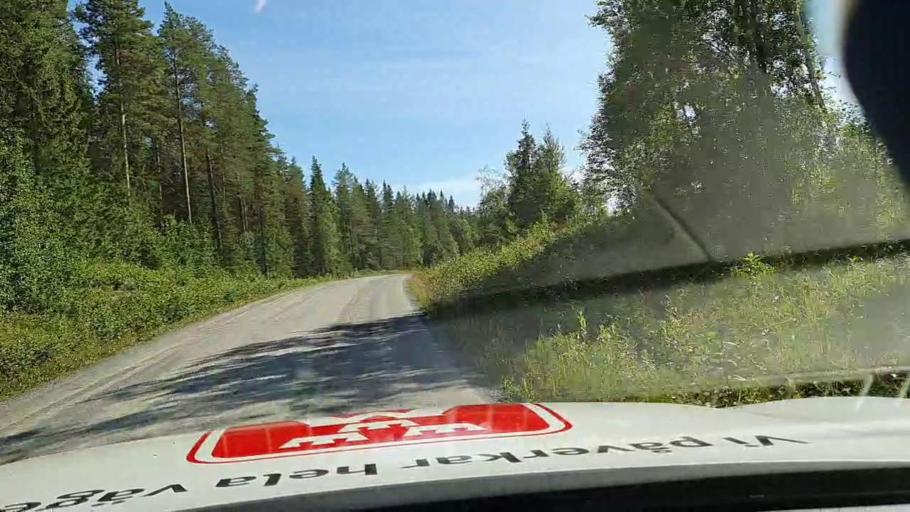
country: SE
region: Jaemtland
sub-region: Krokoms Kommun
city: Krokom
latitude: 63.6845
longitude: 14.5772
